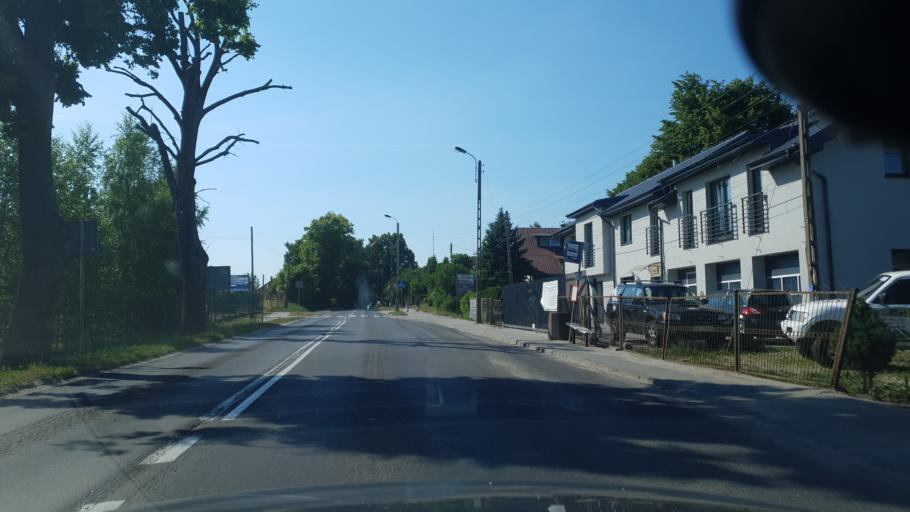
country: PL
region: Pomeranian Voivodeship
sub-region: Gdynia
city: Wielki Kack
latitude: 54.4350
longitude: 18.4661
